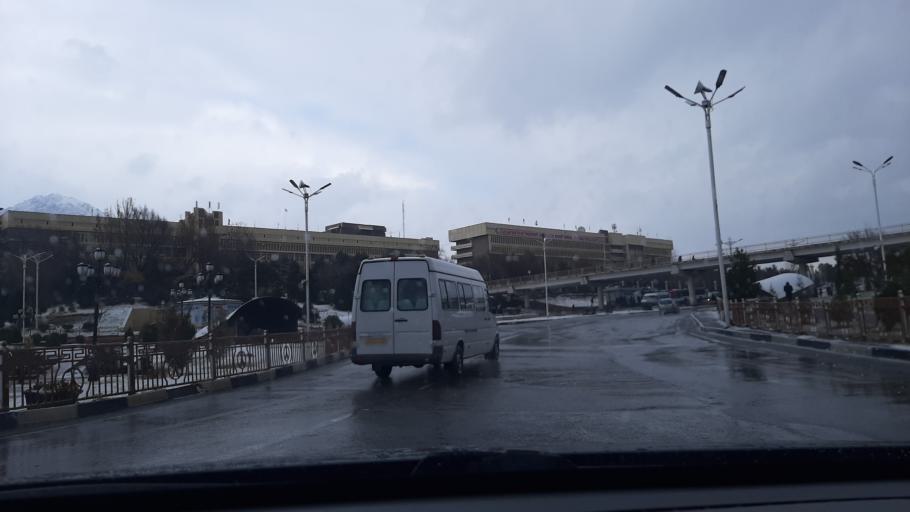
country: TJ
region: Viloyati Sughd
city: Khujand
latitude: 40.3016
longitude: 69.6145
